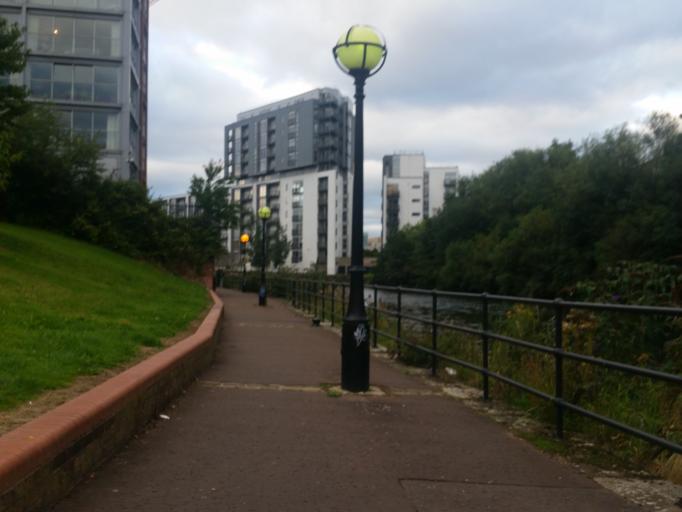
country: GB
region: England
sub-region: Manchester
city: Hulme
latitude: 53.4730
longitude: -2.2652
